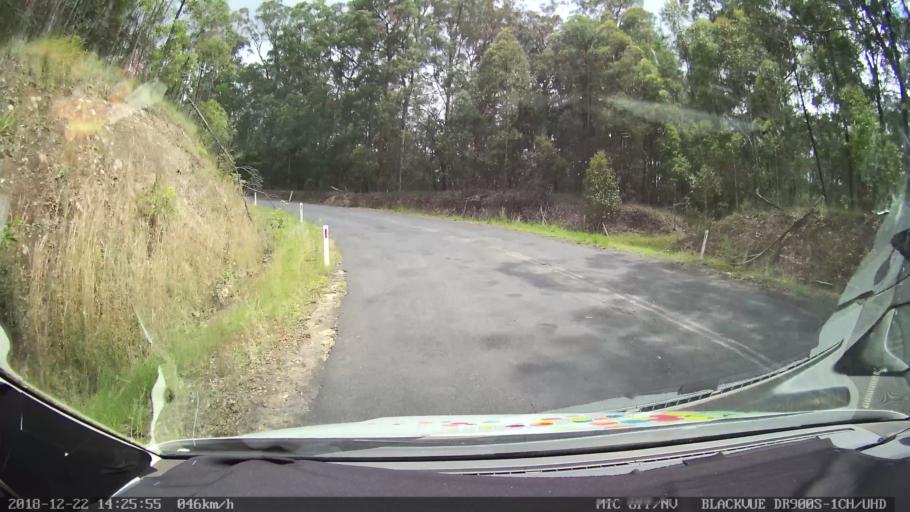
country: AU
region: New South Wales
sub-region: Bellingen
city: Dorrigo
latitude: -30.0547
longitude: 152.6366
